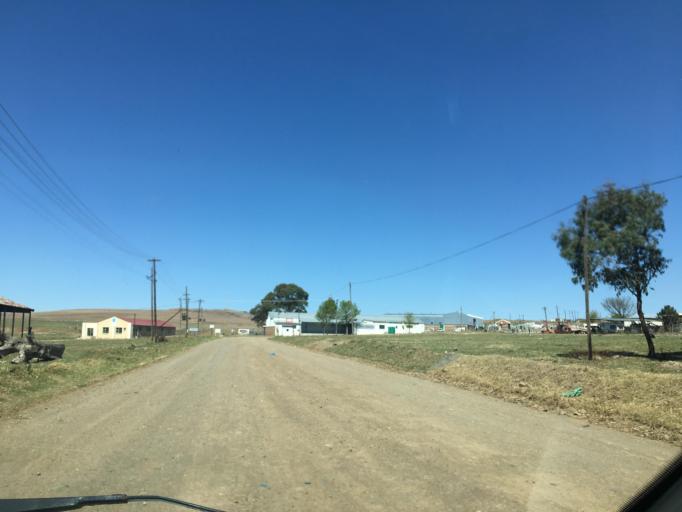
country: ZA
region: Eastern Cape
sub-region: Chris Hani District Municipality
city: Elliot
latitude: -31.3381
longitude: 27.8403
